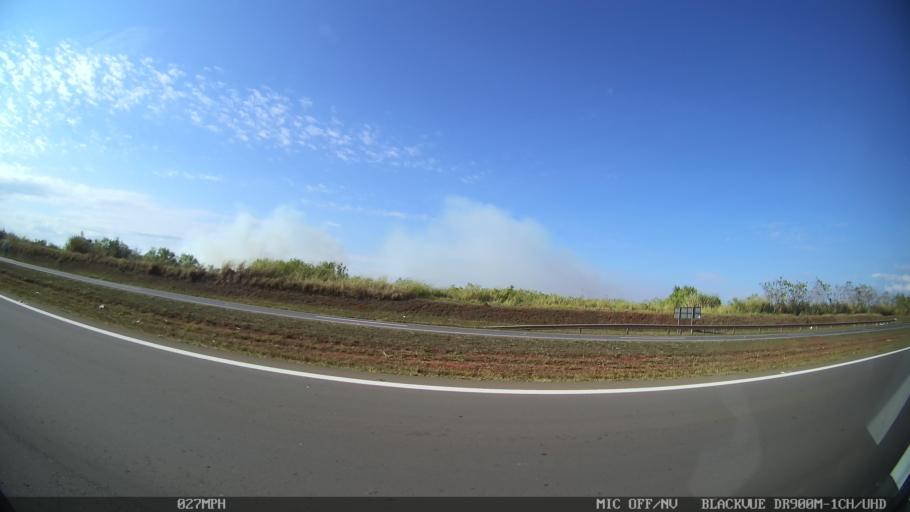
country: BR
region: Sao Paulo
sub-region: Piracicaba
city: Piracicaba
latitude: -22.7140
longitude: -47.6078
